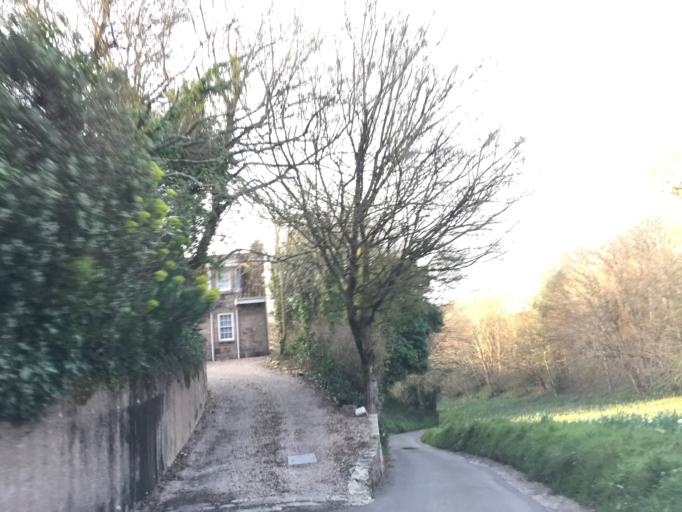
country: JE
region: St Helier
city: Saint Helier
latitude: 49.2307
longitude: -2.0493
